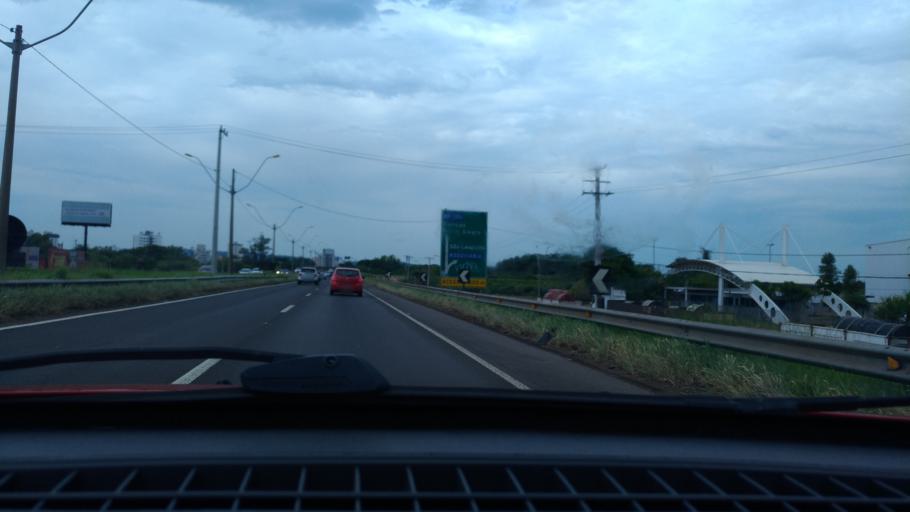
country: BR
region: Rio Grande do Sul
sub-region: Sao Leopoldo
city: Sao Leopoldo
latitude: -29.7551
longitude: -51.1518
